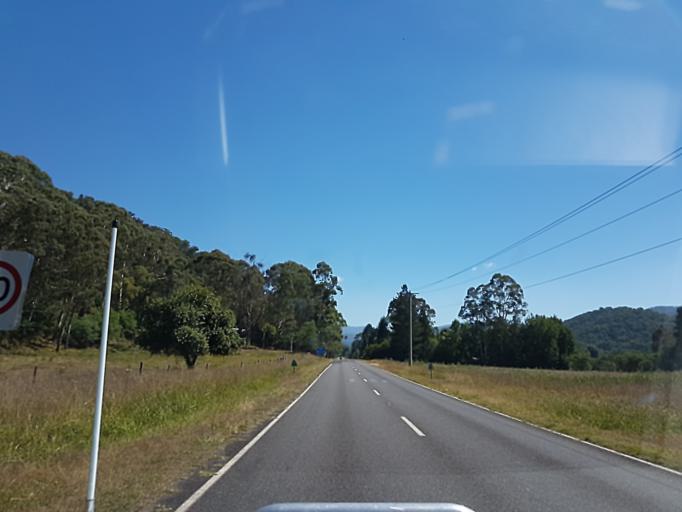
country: AU
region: Victoria
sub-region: Alpine
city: Mount Beauty
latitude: -36.7807
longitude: 147.0346
